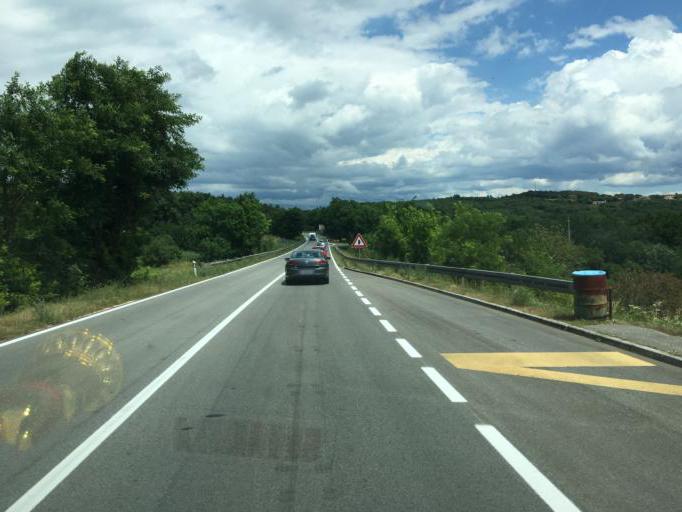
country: HR
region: Istarska
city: Karojba
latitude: 45.2215
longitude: 13.8361
